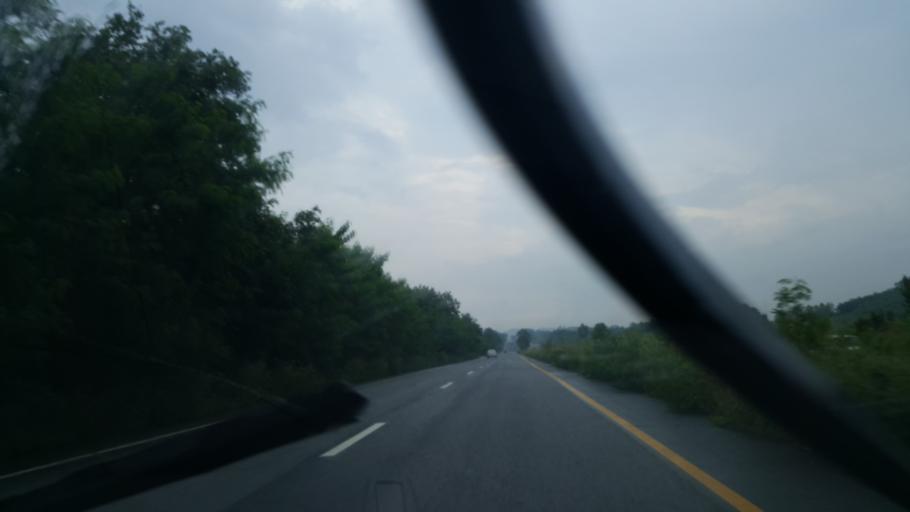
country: TH
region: Rayong
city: Ban Chang
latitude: 12.8417
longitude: 101.0117
